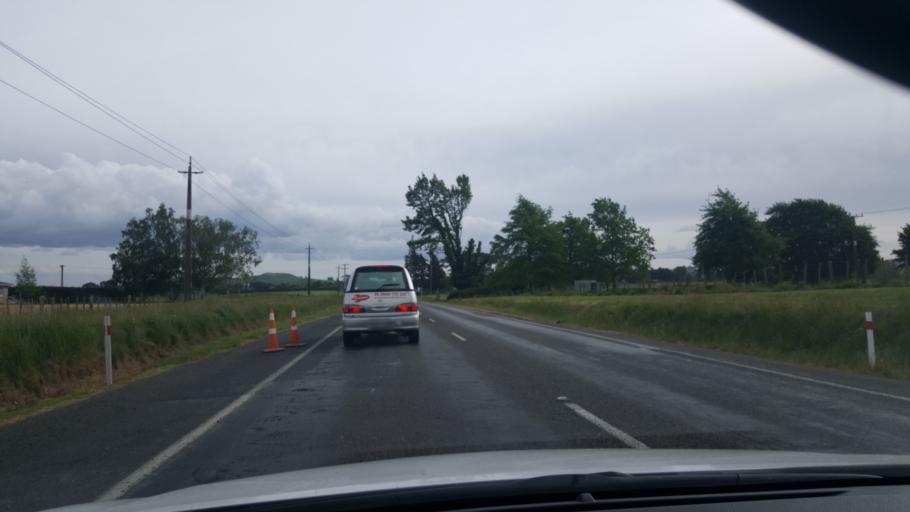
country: NZ
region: Bay of Plenty
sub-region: Rotorua District
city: Rotorua
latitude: -38.4048
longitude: 176.3276
